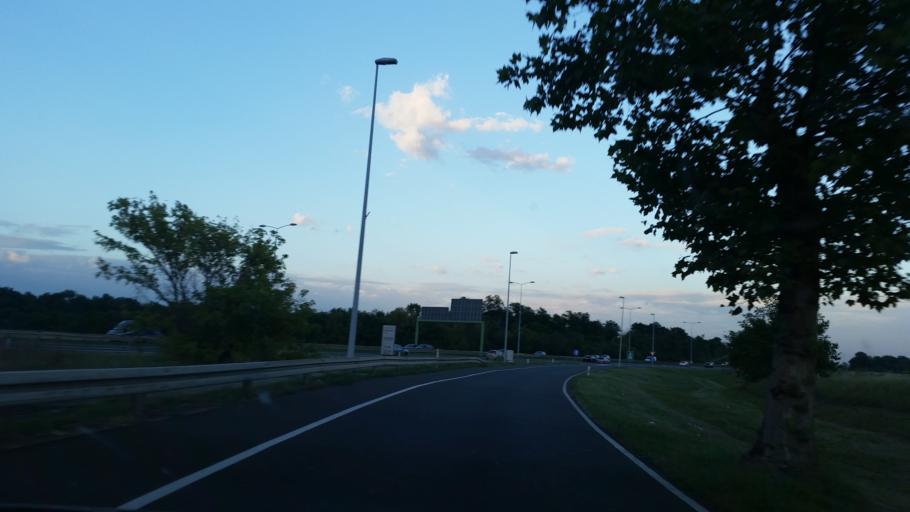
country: RS
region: Central Serbia
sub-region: Belgrade
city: Surcin
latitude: 44.8330
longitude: 20.2813
